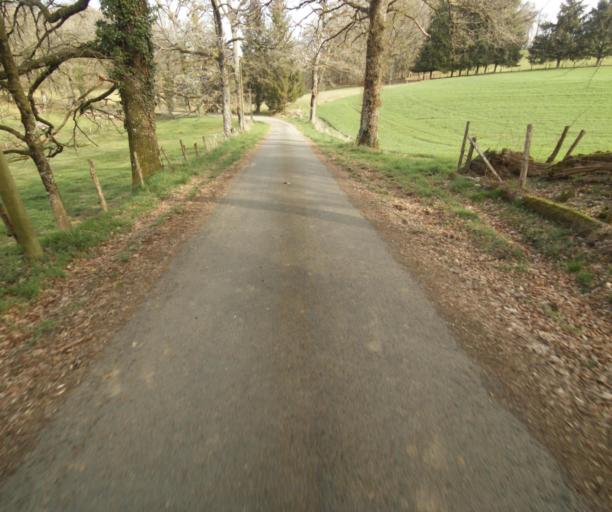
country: FR
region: Limousin
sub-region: Departement de la Correze
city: Chamboulive
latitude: 45.4273
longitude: 1.7594
